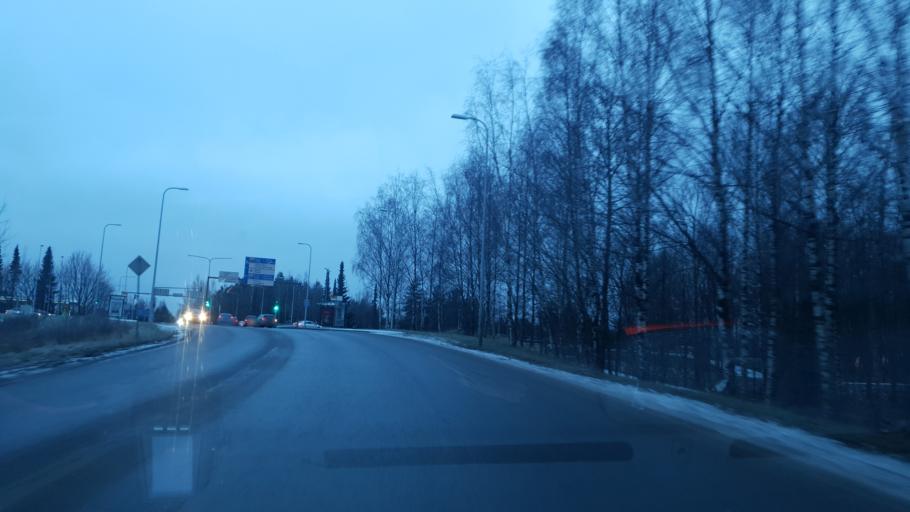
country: FI
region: Uusimaa
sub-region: Helsinki
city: Vantaa
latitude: 60.2433
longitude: 25.0203
